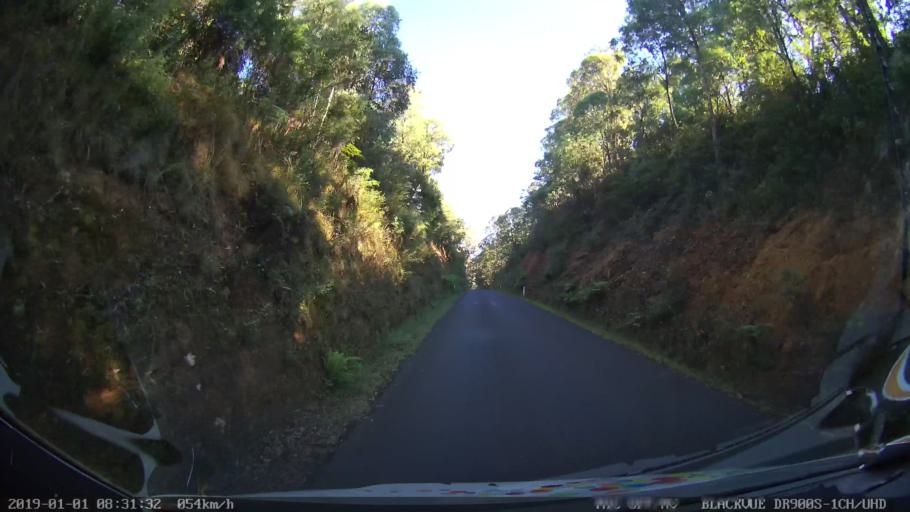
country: AU
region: New South Wales
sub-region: Snowy River
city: Jindabyne
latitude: -36.3694
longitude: 148.2052
